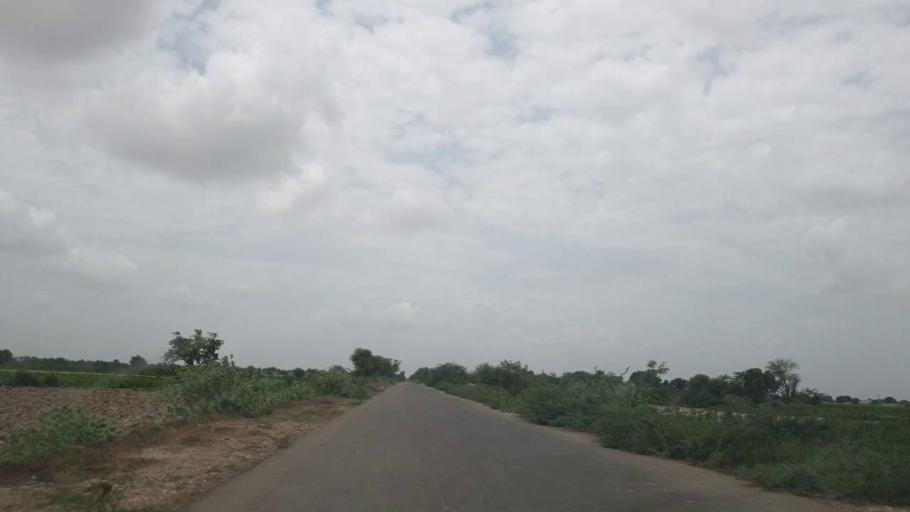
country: PK
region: Sindh
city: Naukot
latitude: 24.9003
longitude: 69.2599
